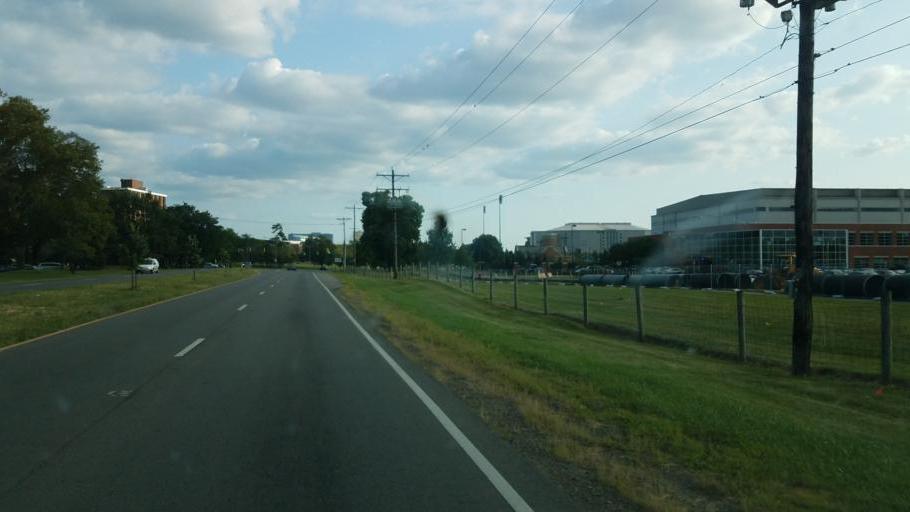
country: US
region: Ohio
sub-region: Franklin County
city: Grandview Heights
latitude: 40.0140
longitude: -83.0225
